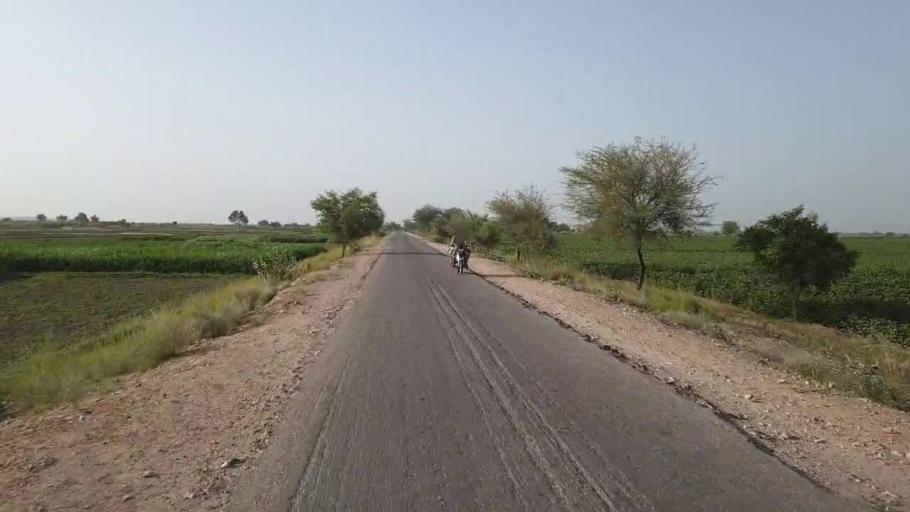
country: PK
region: Sindh
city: Jam Sahib
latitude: 26.4628
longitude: 68.8588
